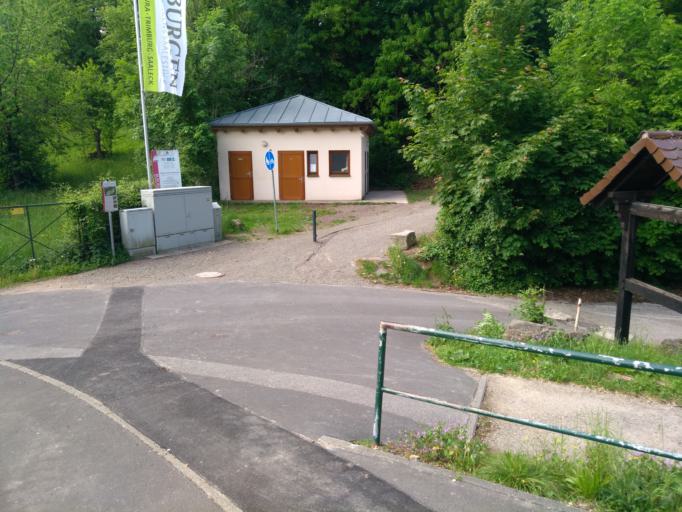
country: DE
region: Bavaria
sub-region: Regierungsbezirk Unterfranken
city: Bad Kissingen
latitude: 50.1892
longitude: 10.0881
